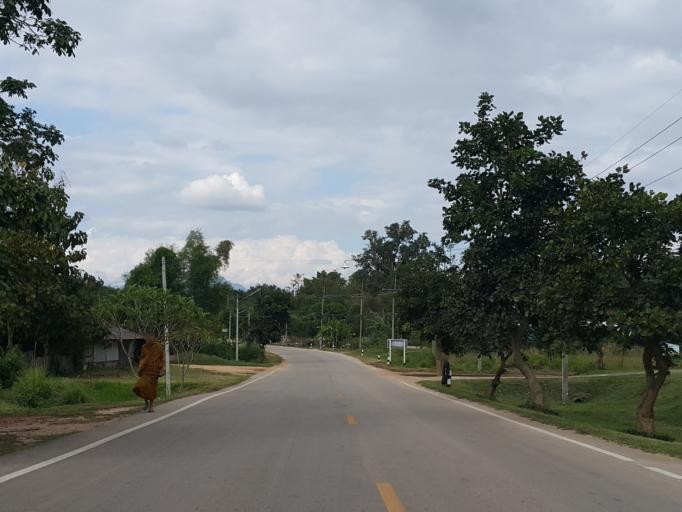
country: TH
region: Lampang
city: Chae Hom
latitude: 18.5671
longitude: 99.4726
